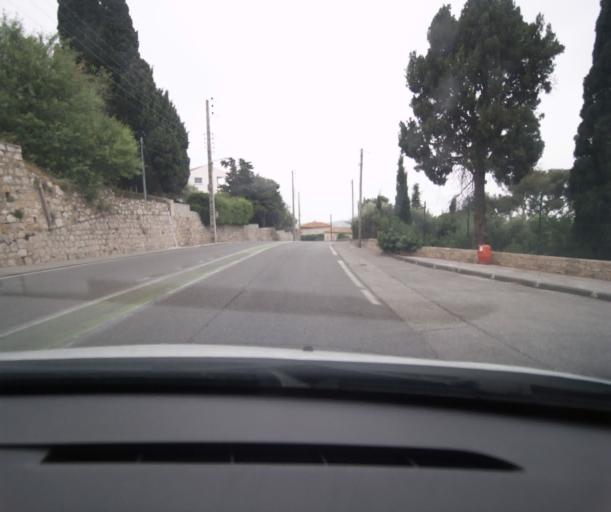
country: FR
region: Provence-Alpes-Cote d'Azur
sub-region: Departement du Var
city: Toulon
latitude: 43.1340
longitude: 5.9487
